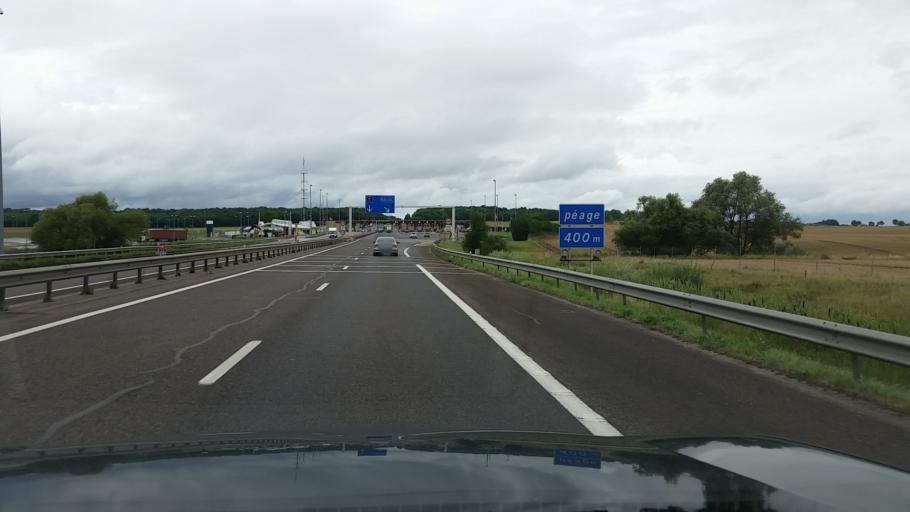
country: FR
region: Lorraine
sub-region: Departement de Meurthe-et-Moselle
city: Dommartin-les-Toul
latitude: 48.6258
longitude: 5.8845
